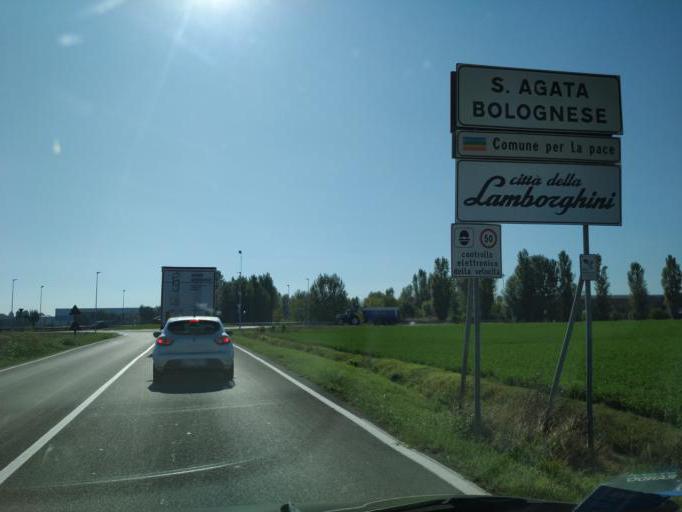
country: IT
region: Emilia-Romagna
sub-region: Provincia di Bologna
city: Sant'Agata Bolognese
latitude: 44.6629
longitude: 11.1156
